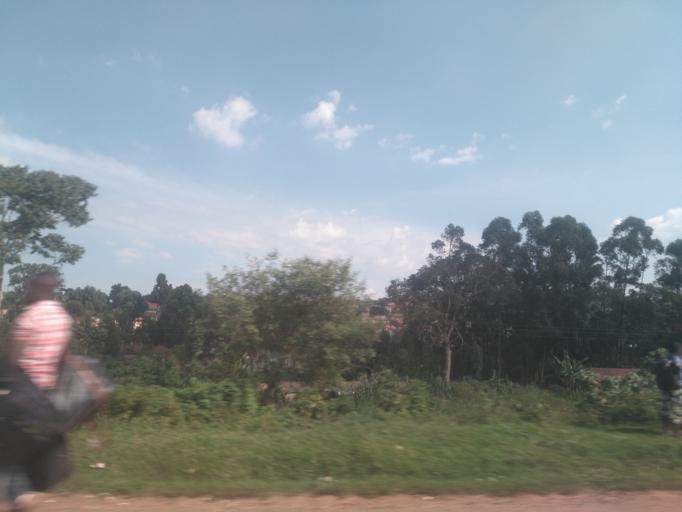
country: UG
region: Central Region
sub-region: Wakiso District
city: Kajansi
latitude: 0.2801
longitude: 32.4825
